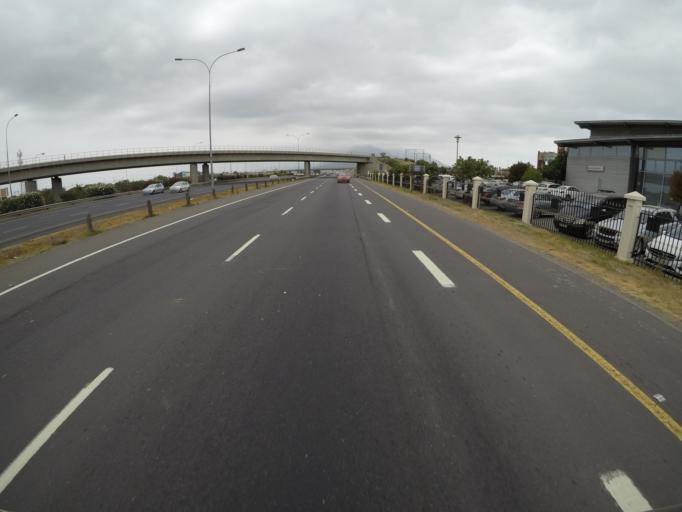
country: ZA
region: Western Cape
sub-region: City of Cape Town
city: Sunset Beach
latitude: -33.8975
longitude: 18.5128
